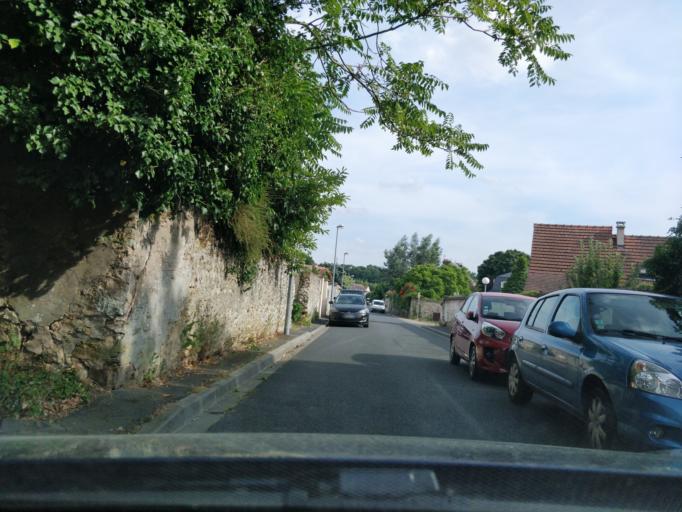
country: FR
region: Ile-de-France
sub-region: Departement de l'Essonne
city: Briis-sous-Forges
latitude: 48.6252
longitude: 2.1211
